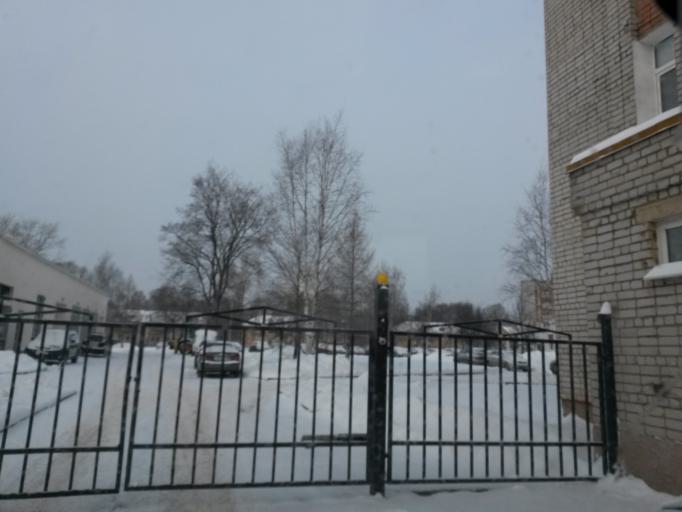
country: RU
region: Jaroslavl
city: Yaroslavl
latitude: 57.6326
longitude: 39.8427
